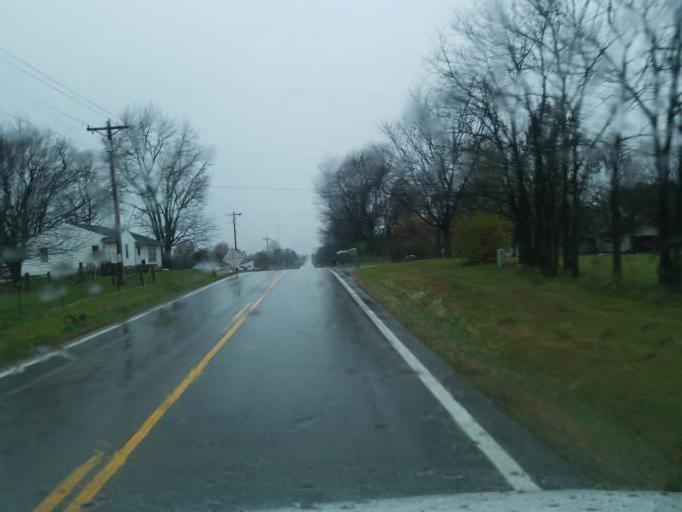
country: US
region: Ohio
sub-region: Delaware County
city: Sunbury
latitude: 40.3250
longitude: -82.8841
